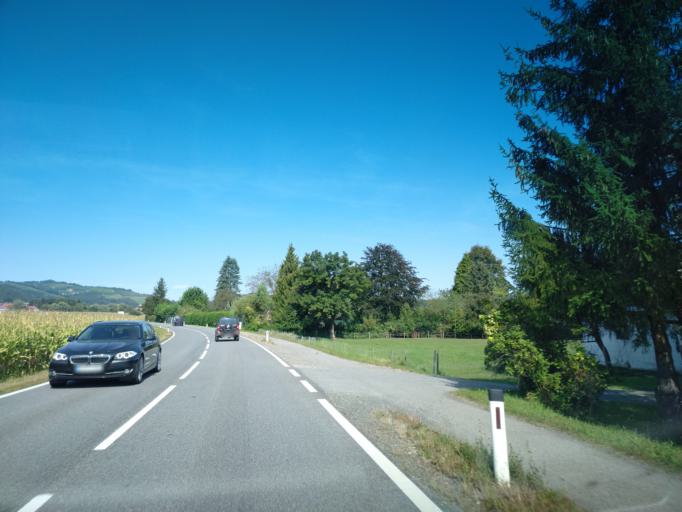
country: AT
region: Styria
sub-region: Politischer Bezirk Leibnitz
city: Heimschuh
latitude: 46.7523
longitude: 15.4766
